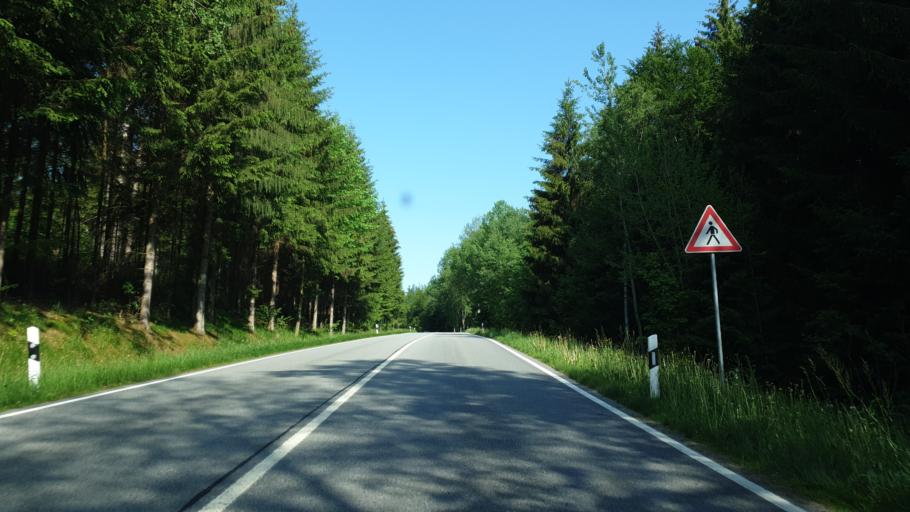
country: DE
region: Saxony
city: Eibenstock
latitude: 50.5090
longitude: 12.6046
